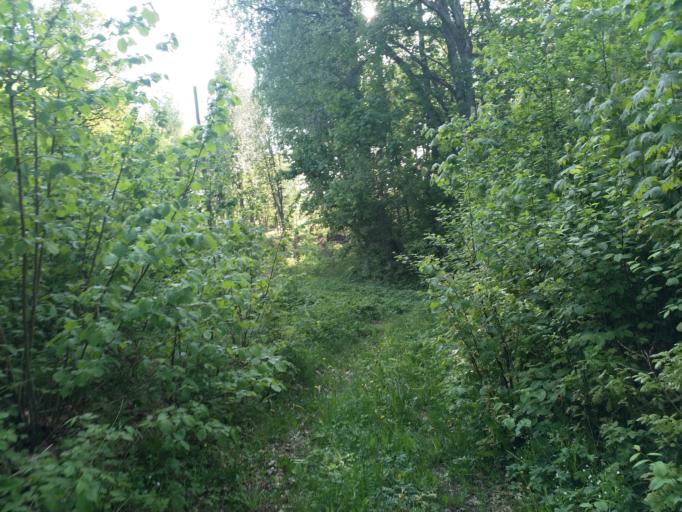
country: LV
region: Kuldigas Rajons
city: Kuldiga
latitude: 56.8583
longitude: 21.8600
